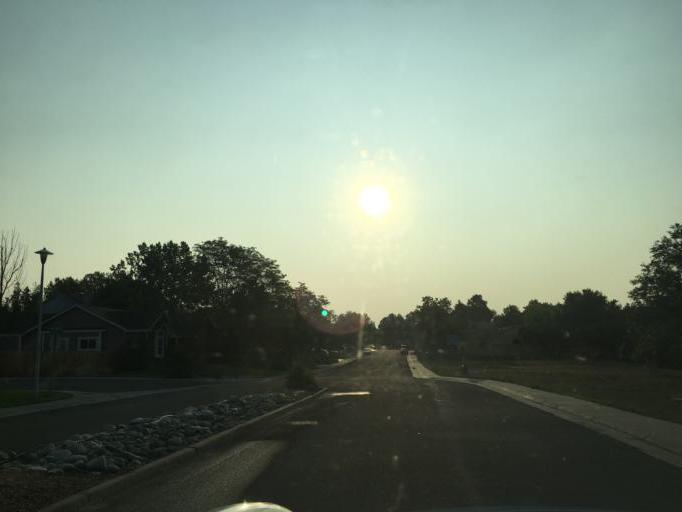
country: US
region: Colorado
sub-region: Adams County
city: Westminster
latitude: 39.8218
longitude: -105.0530
